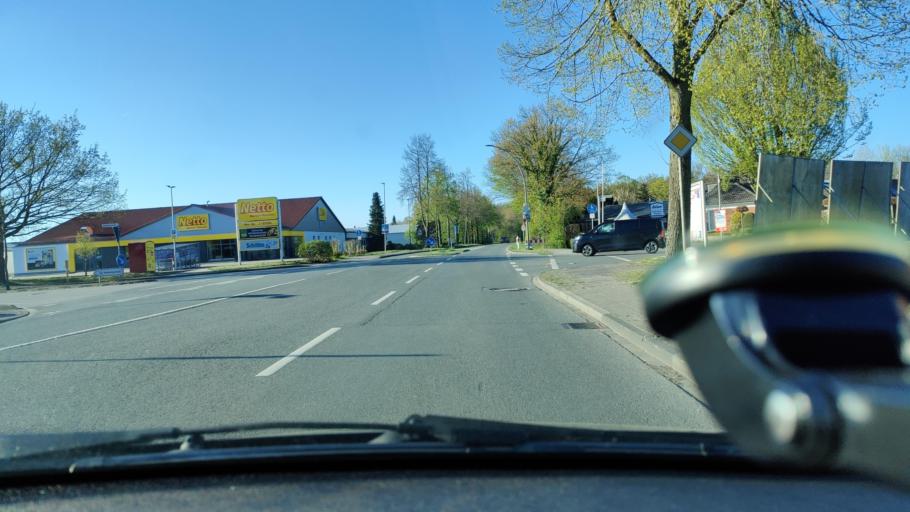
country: DE
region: North Rhine-Westphalia
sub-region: Regierungsbezirk Munster
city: Legden
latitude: 52.0107
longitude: 7.1265
